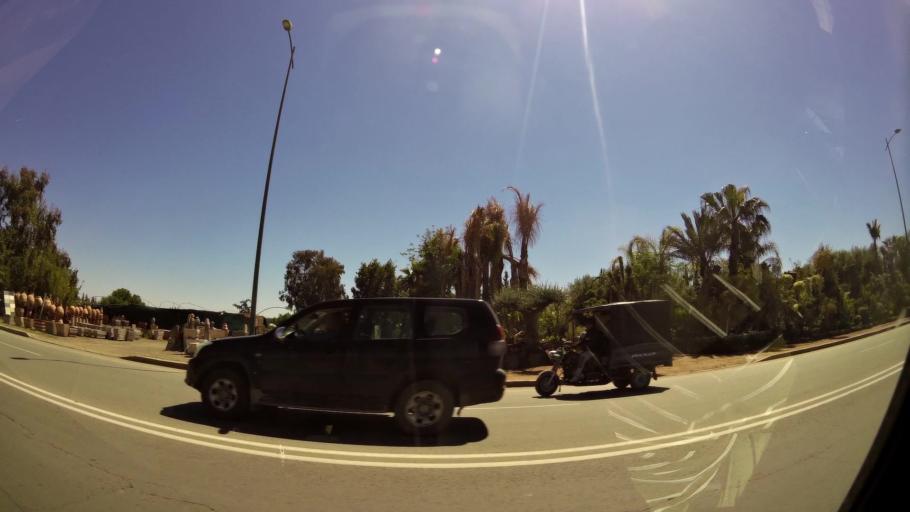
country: MA
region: Marrakech-Tensift-Al Haouz
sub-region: Marrakech
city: Marrakesh
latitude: 31.5676
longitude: -7.9811
